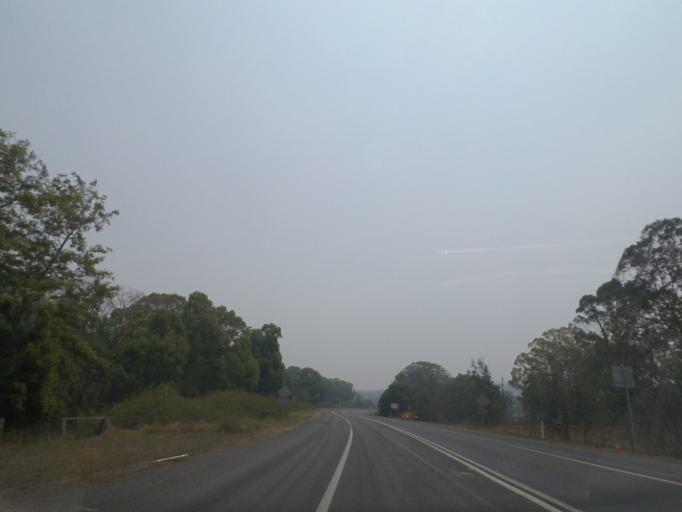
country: AU
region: New South Wales
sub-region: Clarence Valley
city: Maclean
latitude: -29.5474
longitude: 153.1560
